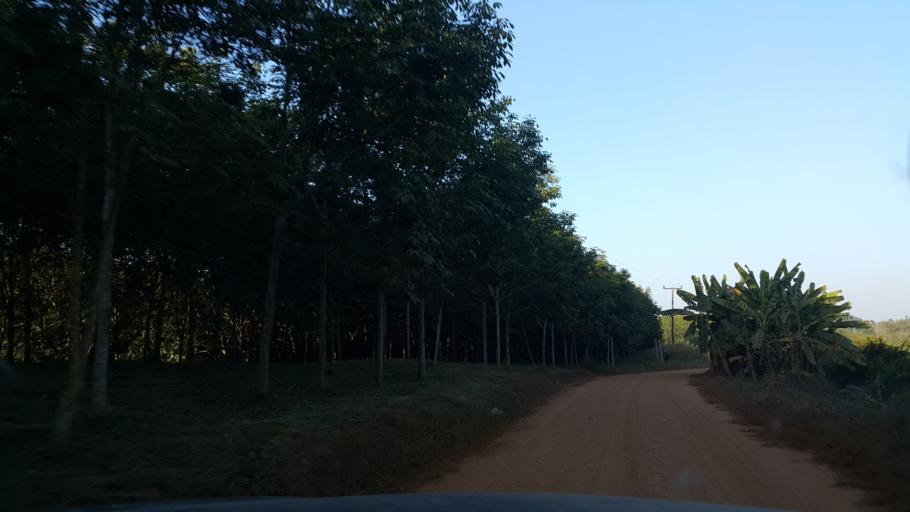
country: TH
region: Sukhothai
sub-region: Amphoe Si Satchanalai
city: Si Satchanalai
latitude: 17.6051
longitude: 99.6151
